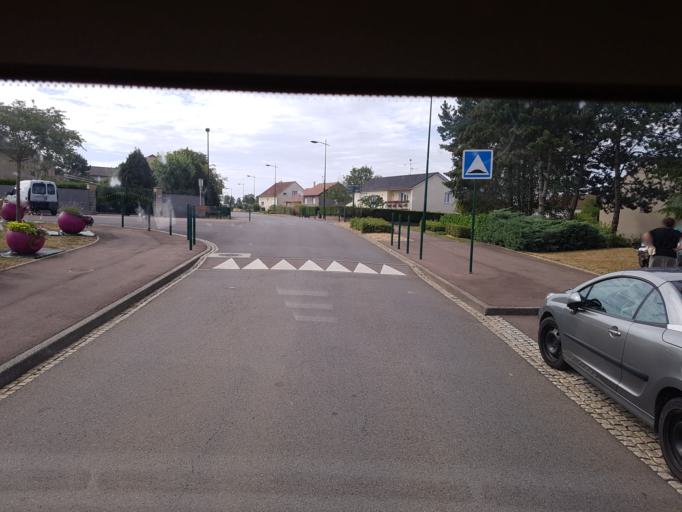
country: FR
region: Lorraine
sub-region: Departement de la Moselle
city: Sainte-Marie-aux-Chenes
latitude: 49.1818
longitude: 5.9985
